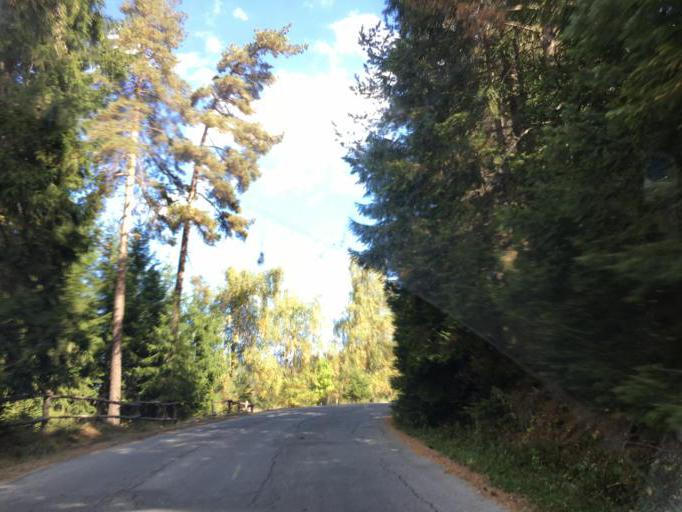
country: BG
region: Pazardzhik
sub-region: Obshtina Batak
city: Batak
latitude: 41.9266
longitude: 24.2771
